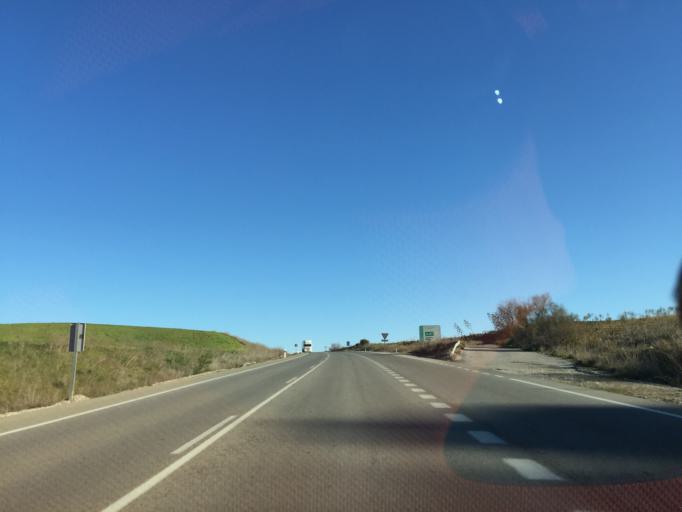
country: ES
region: Andalusia
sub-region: Provincia de Malaga
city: Ardales
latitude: 36.9128
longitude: -4.8417
